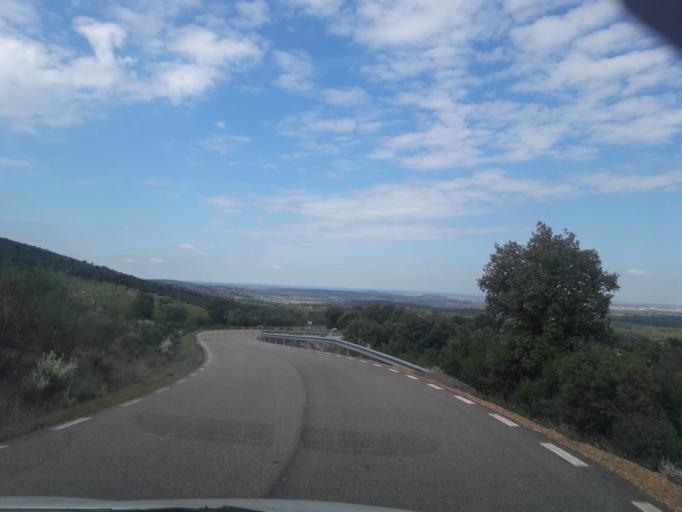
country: ES
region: Castille and Leon
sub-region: Provincia de Salamanca
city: Zamarra
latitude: 40.5498
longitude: -6.4313
